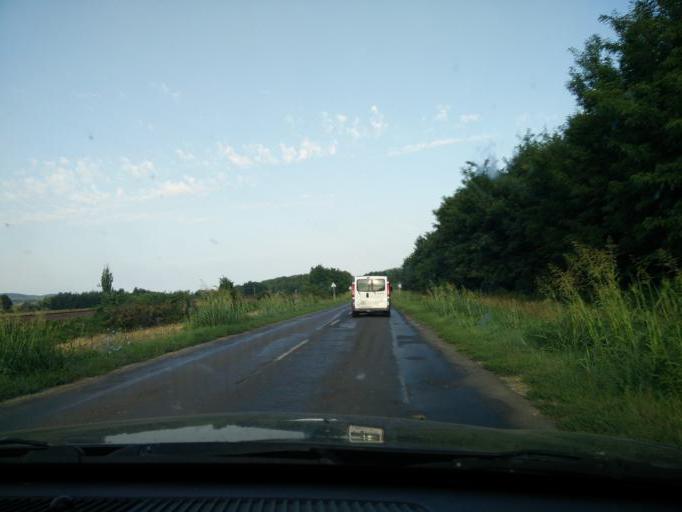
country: HU
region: Tolna
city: Nagymanyok
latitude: 46.2810
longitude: 18.4410
